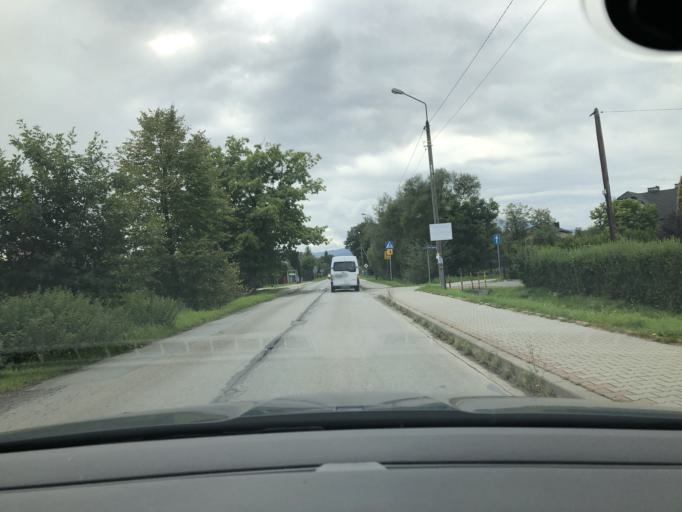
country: PL
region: Silesian Voivodeship
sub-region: Powiat zywiecki
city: Zarzecze
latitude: 49.7176
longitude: 19.1722
